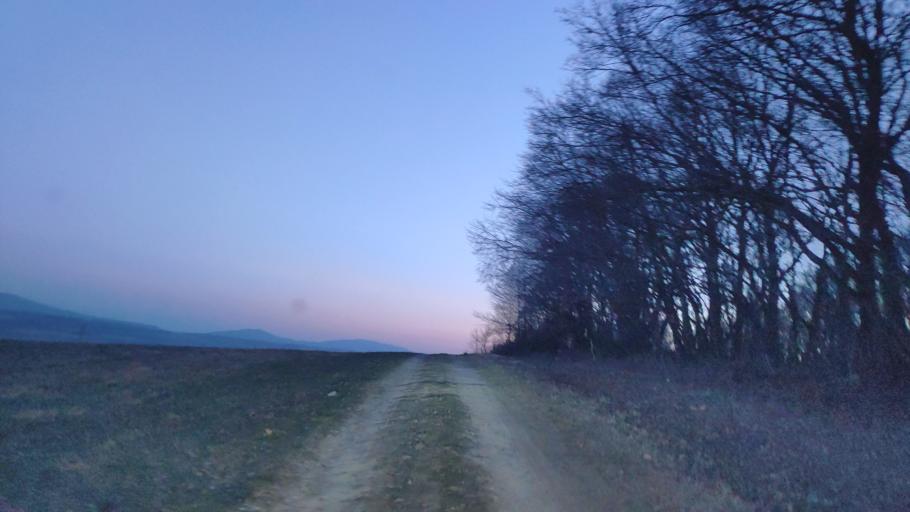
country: SK
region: Kosicky
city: Kosice
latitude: 48.8315
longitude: 21.2601
